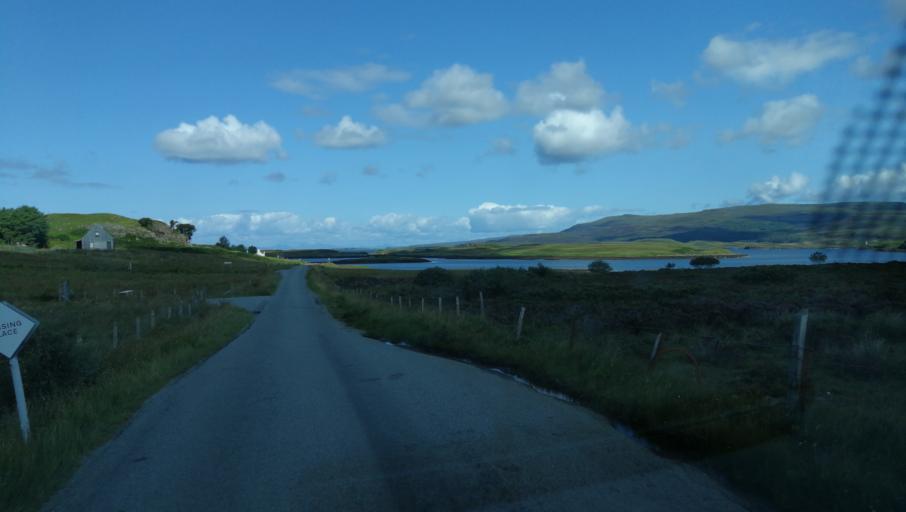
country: GB
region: Scotland
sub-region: Highland
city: Isle of Skye
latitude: 57.4326
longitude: -6.6254
